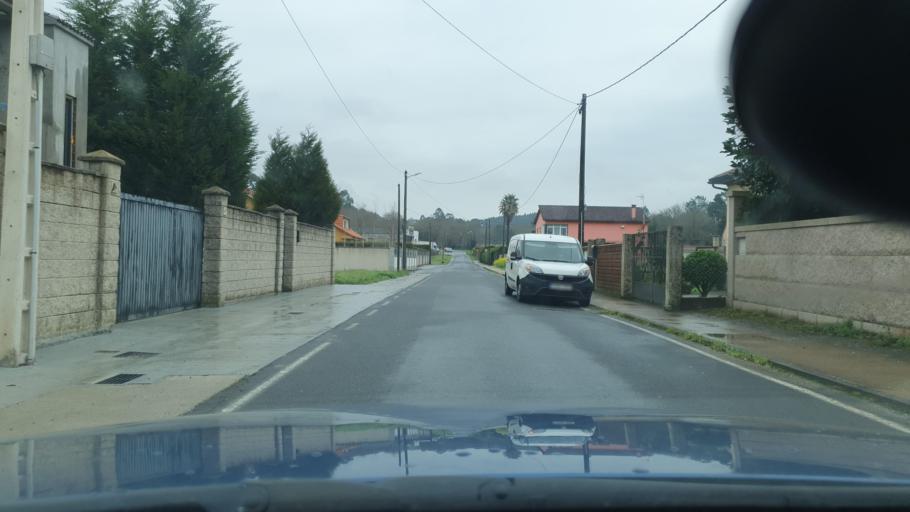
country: ES
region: Galicia
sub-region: Provincia da Coruna
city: Ames
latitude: 42.8284
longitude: -8.6119
